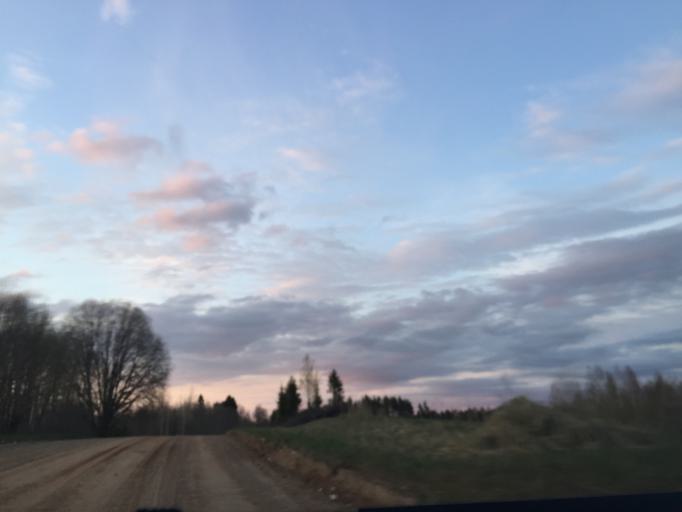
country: LV
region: Aluksnes Rajons
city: Aluksne
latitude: 57.3603
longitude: 26.9893
